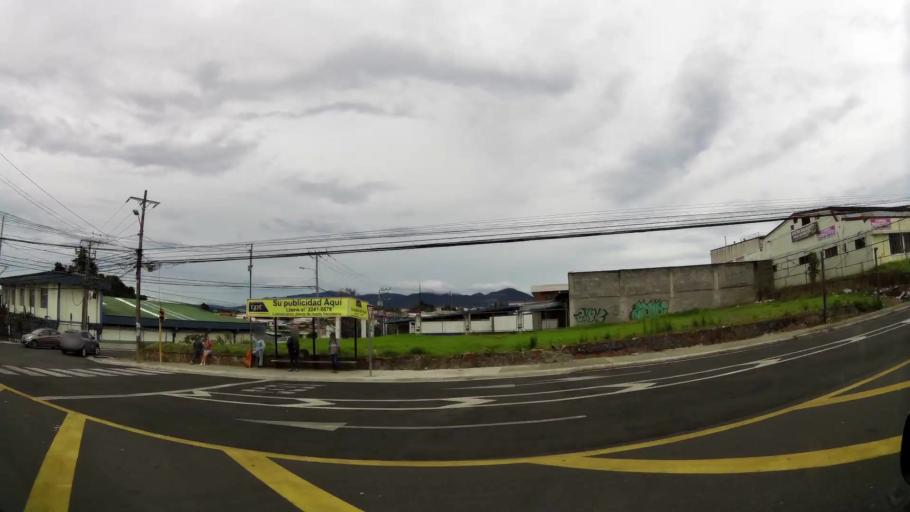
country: CR
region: San Jose
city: Ipis
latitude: 9.9682
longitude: -84.0193
